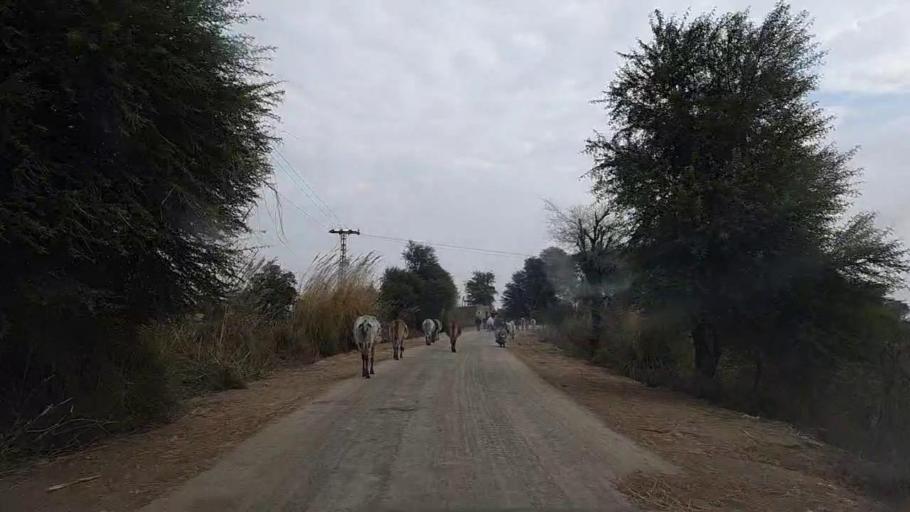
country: PK
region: Sindh
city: Sanghar
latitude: 26.2298
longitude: 68.9969
